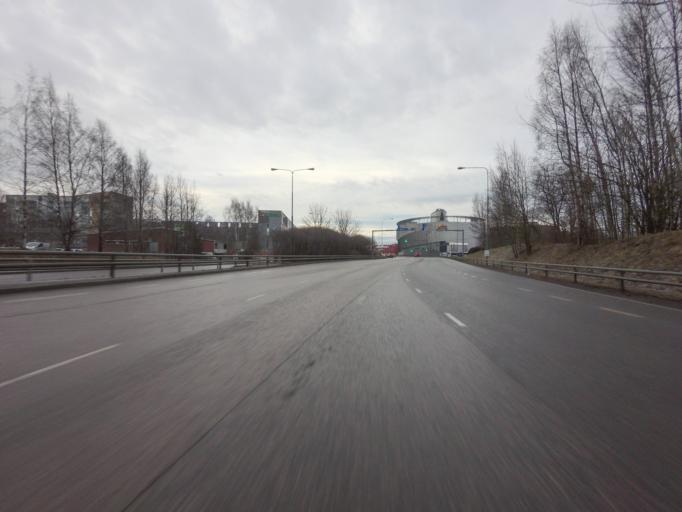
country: FI
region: Uusimaa
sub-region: Helsinki
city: Vantaa
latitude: 60.2152
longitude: 25.0851
